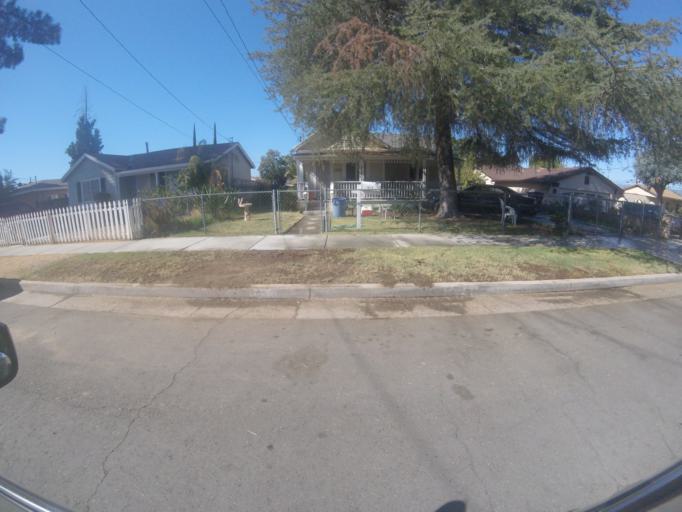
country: US
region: California
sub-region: San Bernardino County
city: Redlands
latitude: 34.0658
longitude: -117.1792
